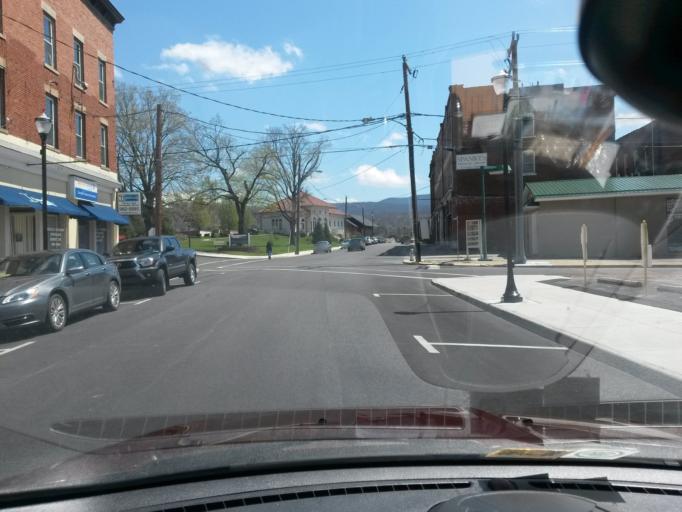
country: US
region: Virginia
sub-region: City of Covington
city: Covington
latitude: 37.7896
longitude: -79.9950
